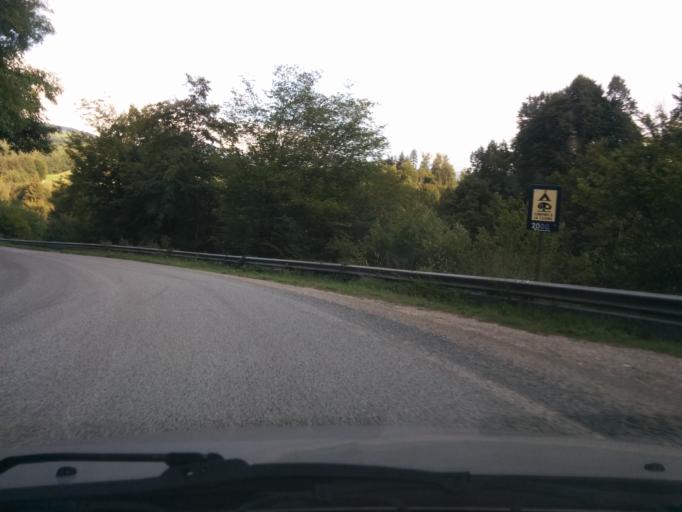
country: FR
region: Rhone-Alpes
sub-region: Departement de la Savoie
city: Saint-Beron
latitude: 45.4732
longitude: 5.7354
